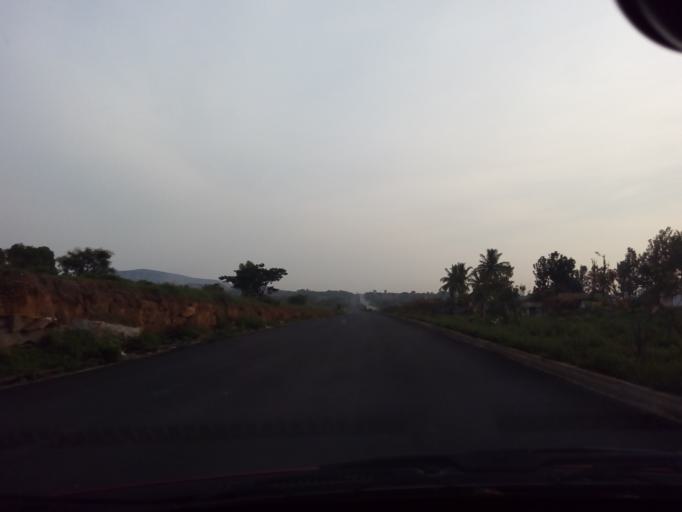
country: IN
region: Karnataka
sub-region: Chikkaballapur
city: Gudibanda
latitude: 13.5942
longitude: 77.7849
